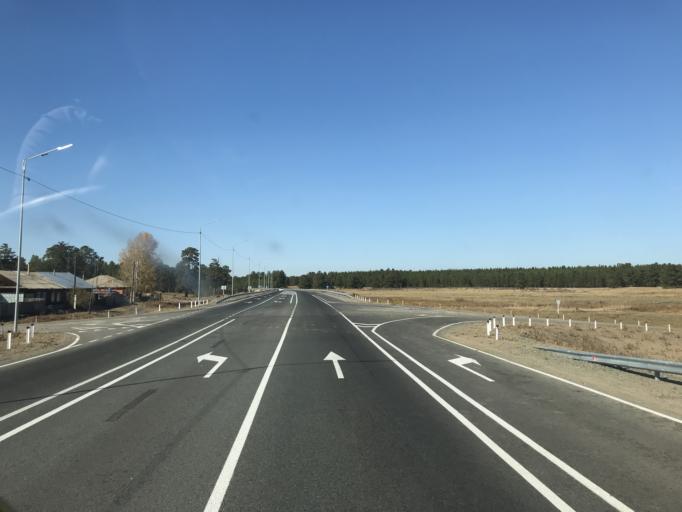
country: KZ
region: East Kazakhstan
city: Semey
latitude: 50.8028
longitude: 79.5380
